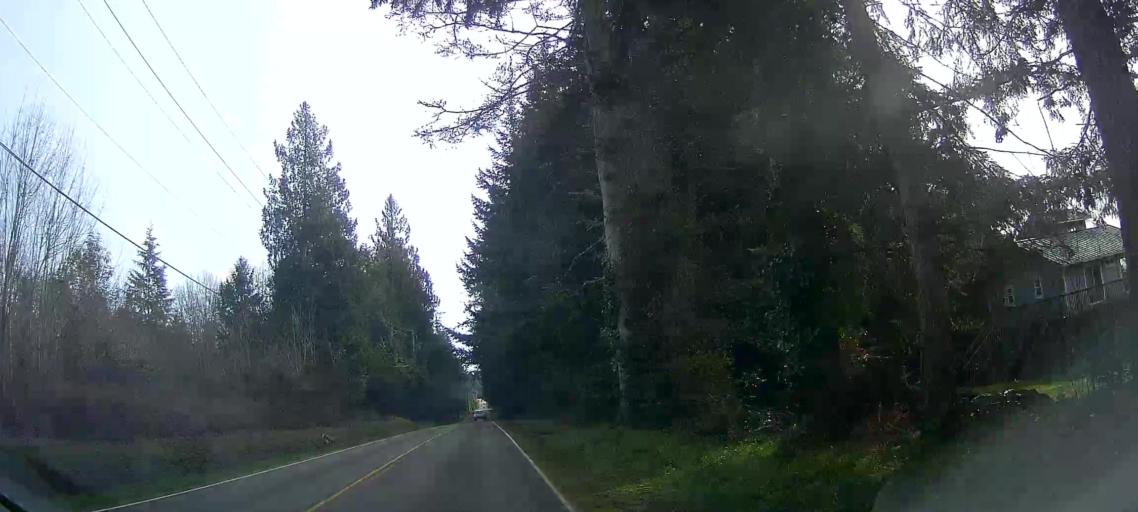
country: US
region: Washington
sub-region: Island County
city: Langley
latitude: 48.1009
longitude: -122.4167
